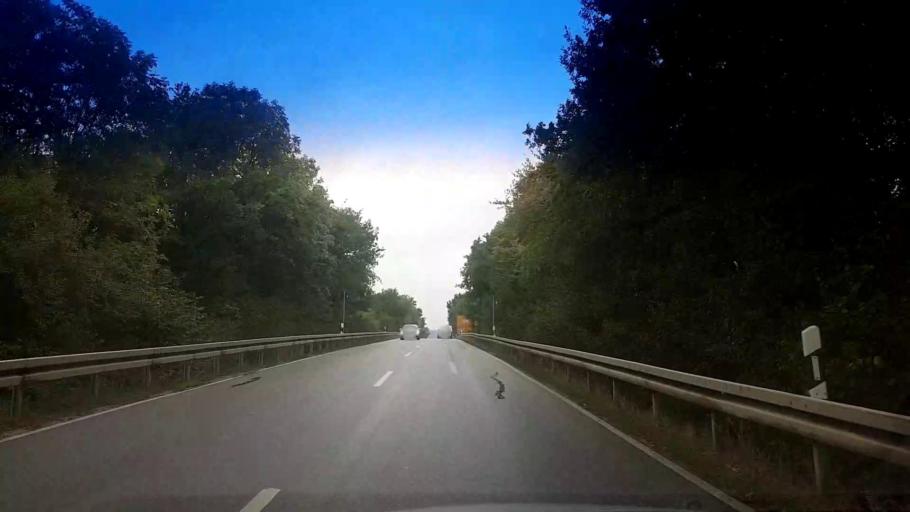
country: DE
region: Bavaria
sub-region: Upper Franconia
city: Eggolsheim
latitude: 49.7724
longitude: 11.0410
